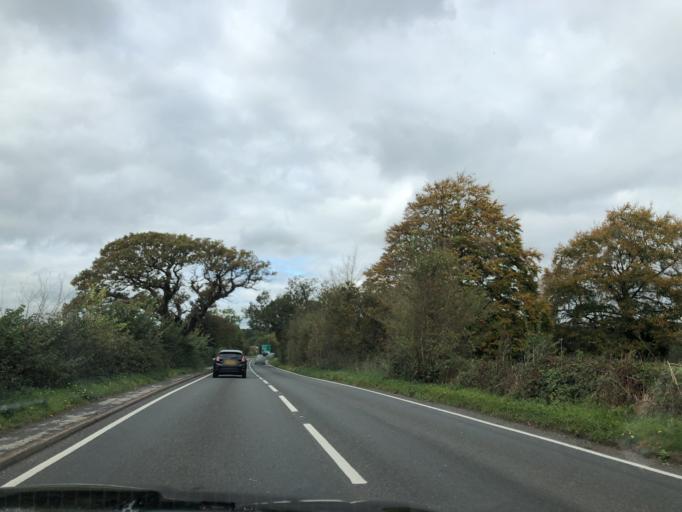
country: GB
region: England
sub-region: Warwickshire
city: Royal Leamington Spa
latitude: 52.3229
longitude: -1.5506
